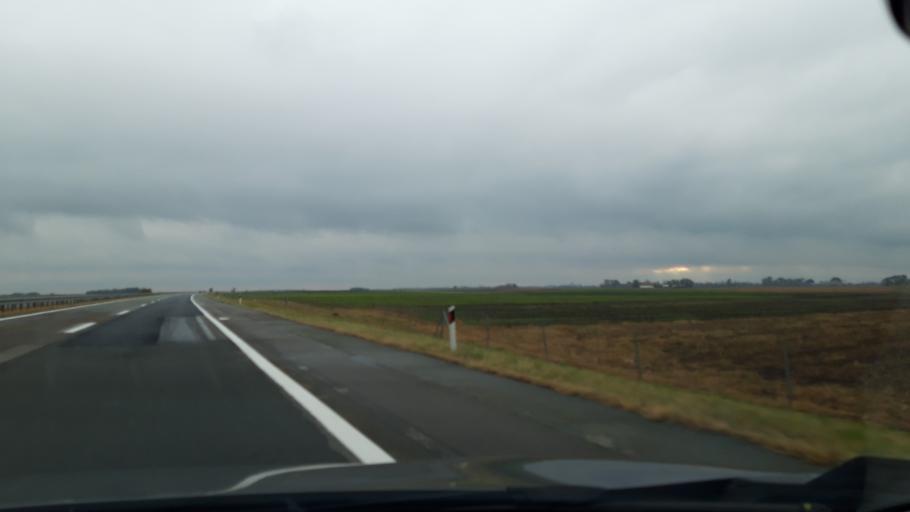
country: RS
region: Autonomna Pokrajina Vojvodina
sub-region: Severnobacki Okrug
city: Backa Topola
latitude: 45.8653
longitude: 19.6996
